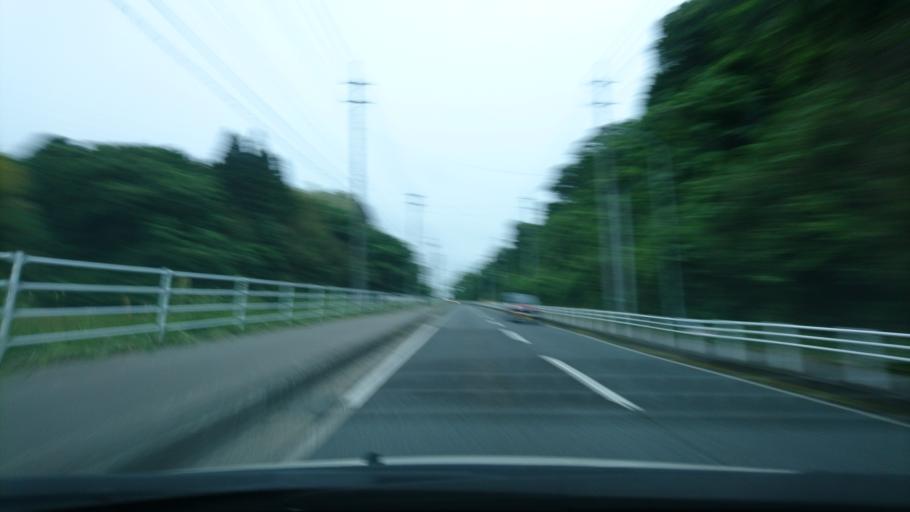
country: JP
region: Iwate
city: Ichinoseki
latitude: 38.9211
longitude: 141.1492
